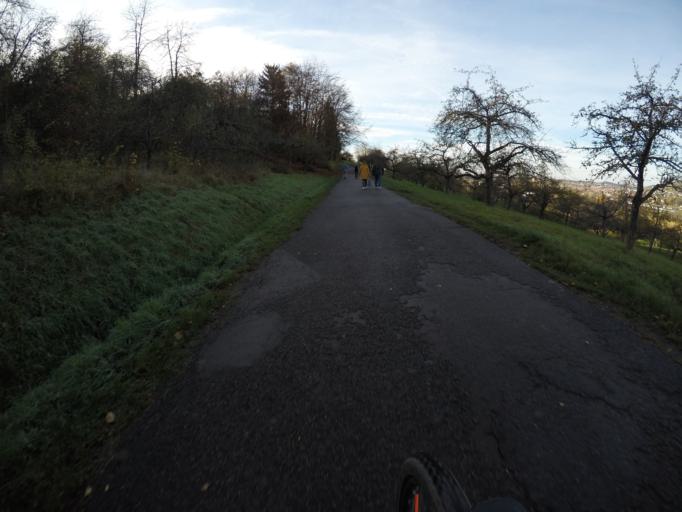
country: DE
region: Baden-Wuerttemberg
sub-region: Regierungsbezirk Stuttgart
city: Weinstadt-Endersbach
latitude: 48.8080
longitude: 9.3994
